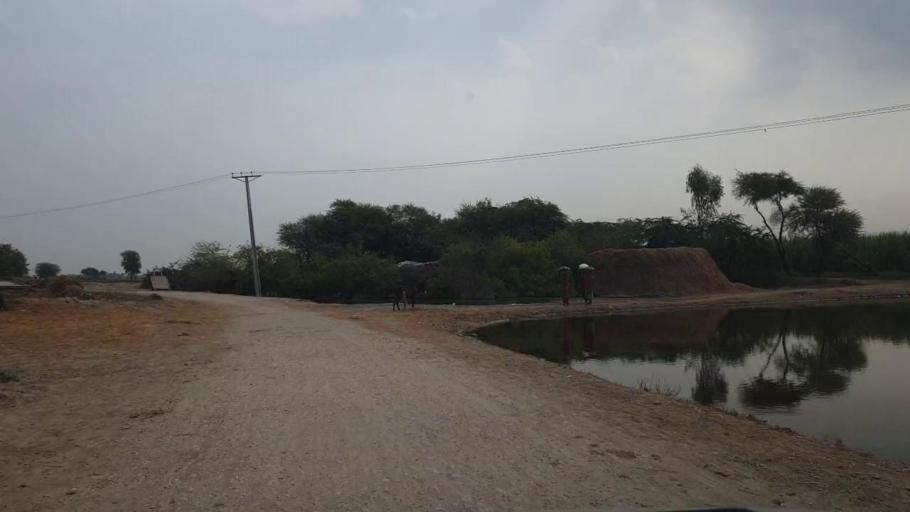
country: PK
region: Sindh
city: Matli
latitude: 24.9557
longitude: 68.7123
